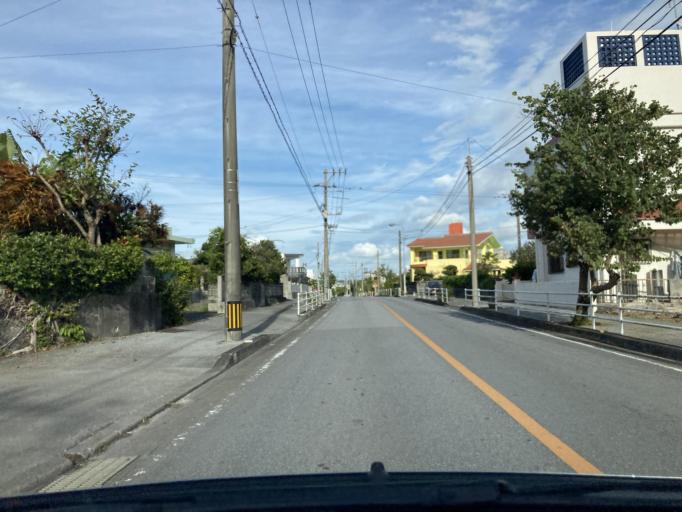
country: JP
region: Okinawa
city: Itoman
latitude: 26.1324
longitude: 127.7249
